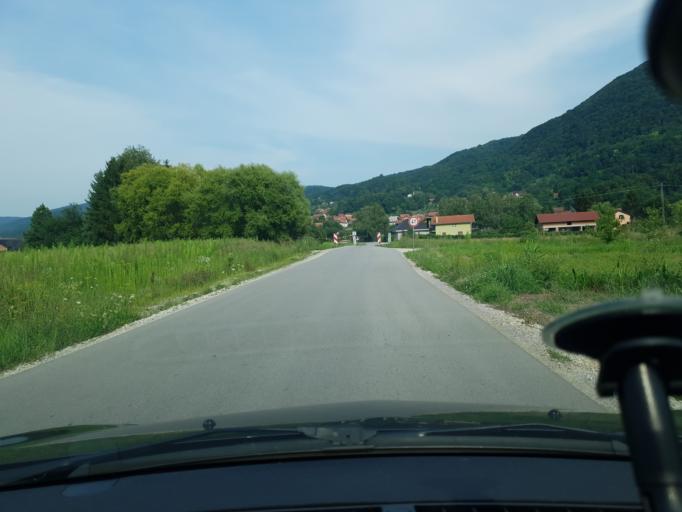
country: HR
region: Zagrebacka
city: Jablanovec
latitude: 45.8771
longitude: 15.8420
